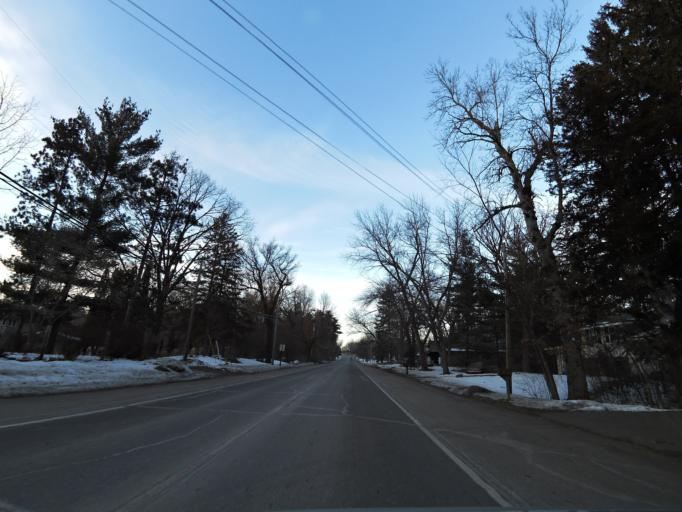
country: US
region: Minnesota
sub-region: Washington County
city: Lake Elmo
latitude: 44.9930
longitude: -92.8794
